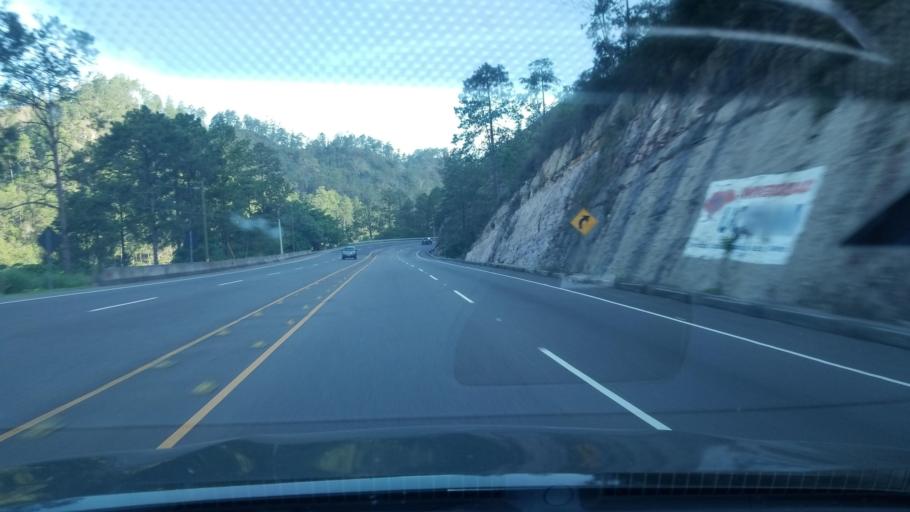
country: HN
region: Comayagua
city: El Sauce
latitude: 14.5190
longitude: -87.7607
